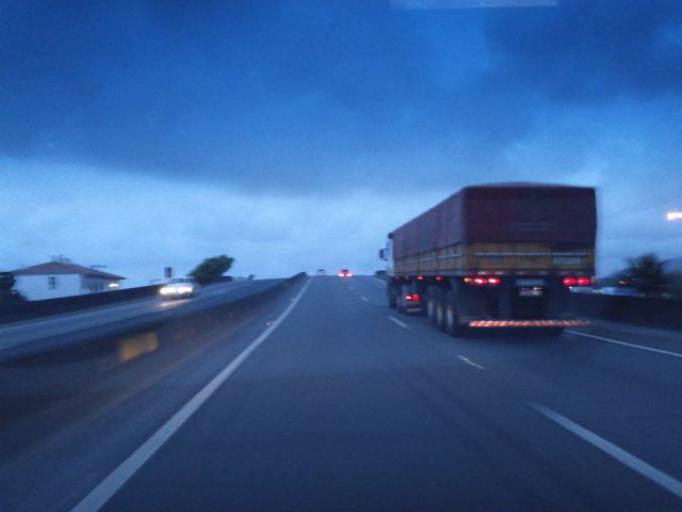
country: BR
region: Santa Catarina
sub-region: Barra Velha
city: Barra Velha
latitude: -26.6501
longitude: -48.6869
